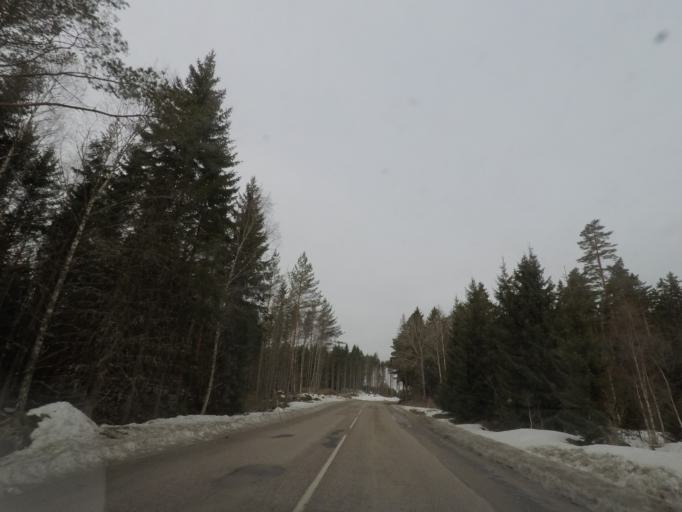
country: SE
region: Vaestmanland
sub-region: Vasteras
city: Skultuna
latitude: 59.7407
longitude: 16.3863
